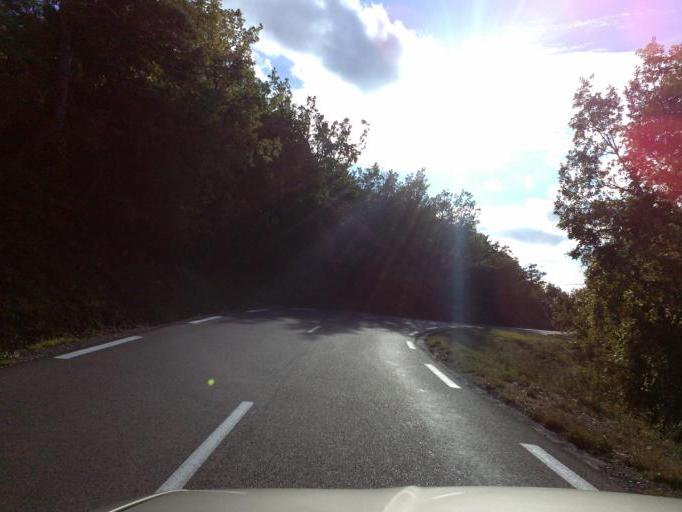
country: FR
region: Provence-Alpes-Cote d'Azur
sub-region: Departement des Alpes-de-Haute-Provence
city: Riez
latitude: 43.8991
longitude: 6.1374
